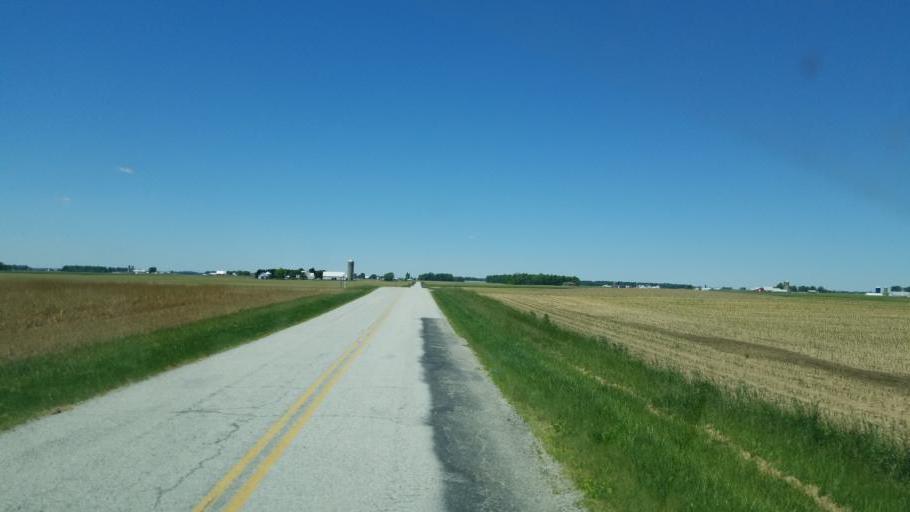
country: US
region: Ohio
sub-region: Auglaize County
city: Minster
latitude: 40.3856
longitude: -84.4401
